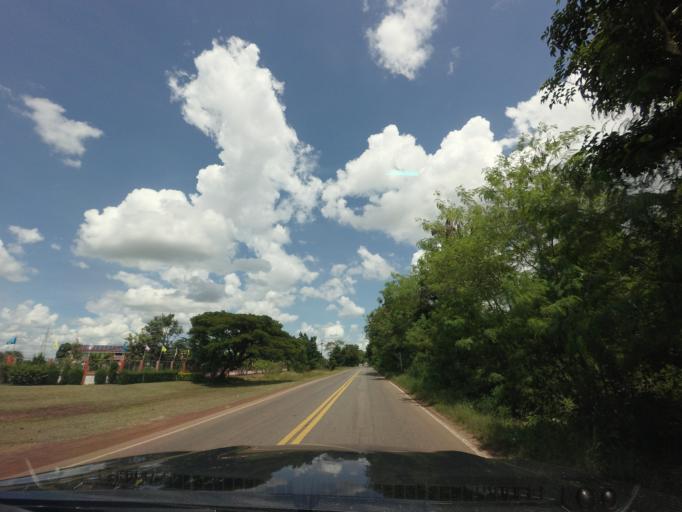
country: TH
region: Changwat Udon Thani
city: Ban Dung
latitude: 17.6707
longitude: 103.1699
